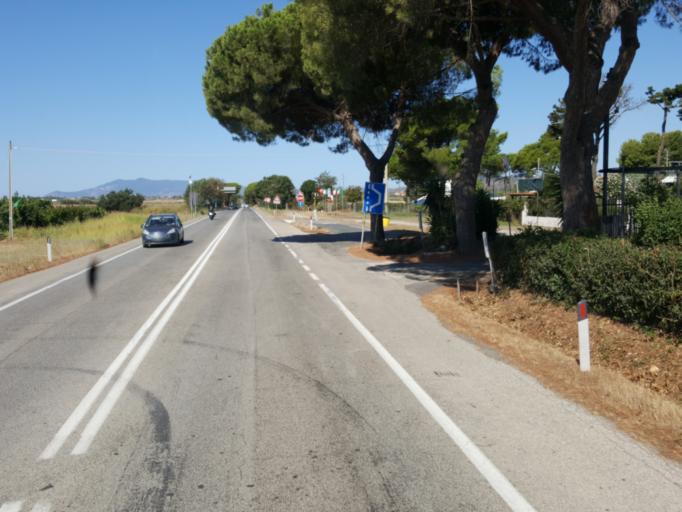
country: IT
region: Tuscany
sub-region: Provincia di Grosseto
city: Capalbio
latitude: 42.4144
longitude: 11.4457
